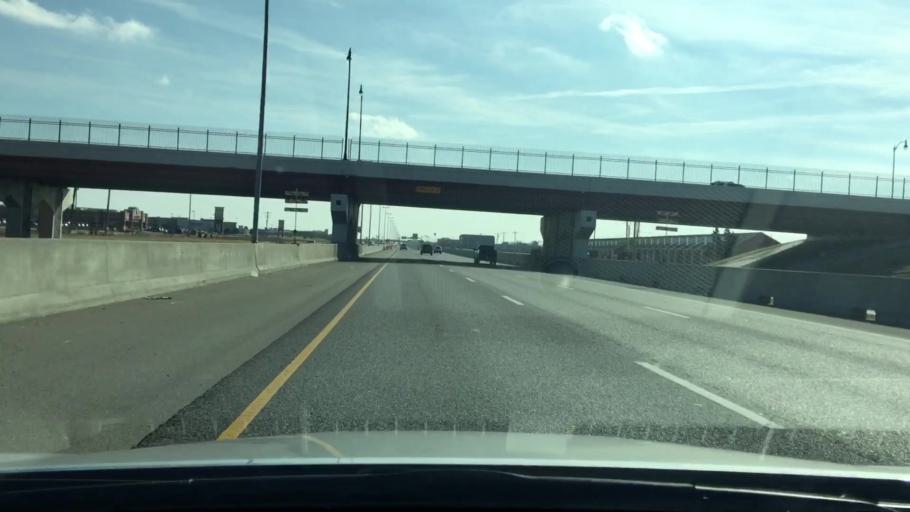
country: US
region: Oklahoma
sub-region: Cleveland County
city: Norman
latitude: 35.2485
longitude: -97.4856
